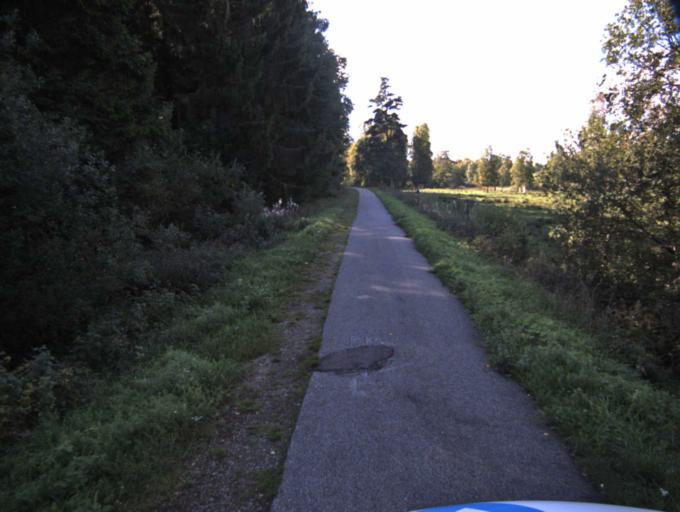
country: SE
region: Vaestra Goetaland
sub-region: Ulricehamns Kommun
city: Ulricehamn
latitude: 57.8397
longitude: 13.2738
